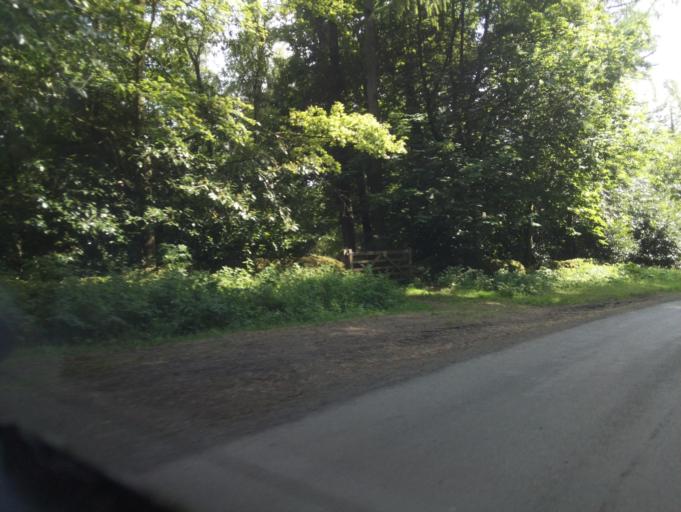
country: GB
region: England
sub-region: Wiltshire
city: Luckington
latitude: 51.5784
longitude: -2.2717
